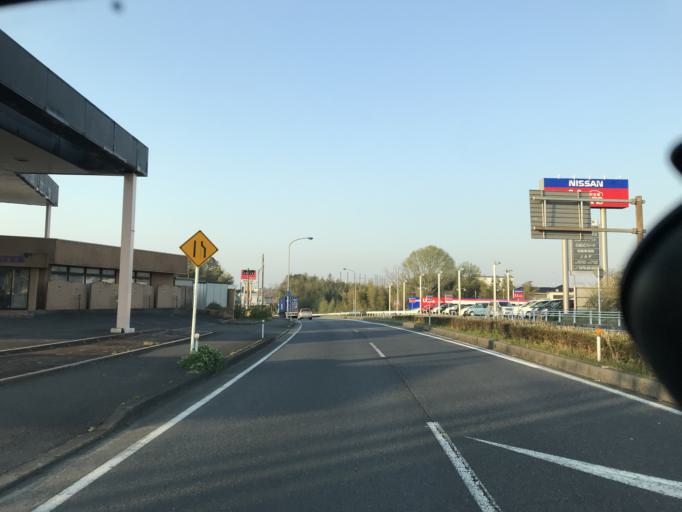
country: JP
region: Chiba
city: Narita
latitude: 35.7600
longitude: 140.3041
